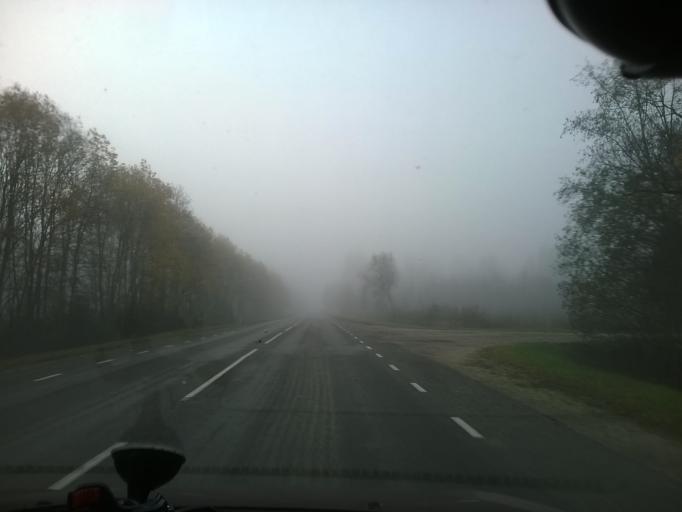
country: EE
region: Tartu
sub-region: Elva linn
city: Elva
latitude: 58.1229
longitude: 26.5185
